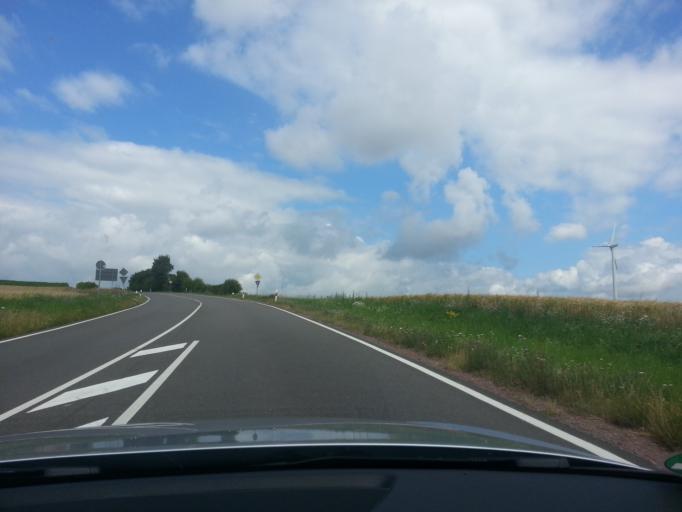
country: DE
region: Rheinland-Pfalz
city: Kirf
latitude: 49.5161
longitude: 6.4520
